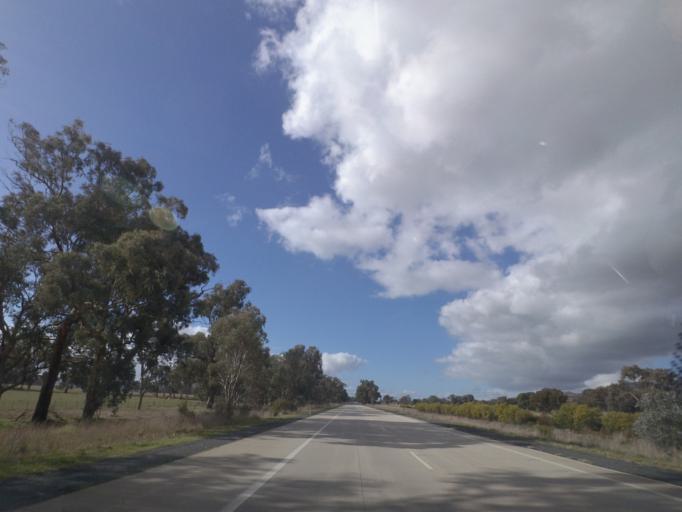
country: AU
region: New South Wales
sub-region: Greater Hume Shire
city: Holbrook
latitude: -35.6923
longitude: 147.3459
